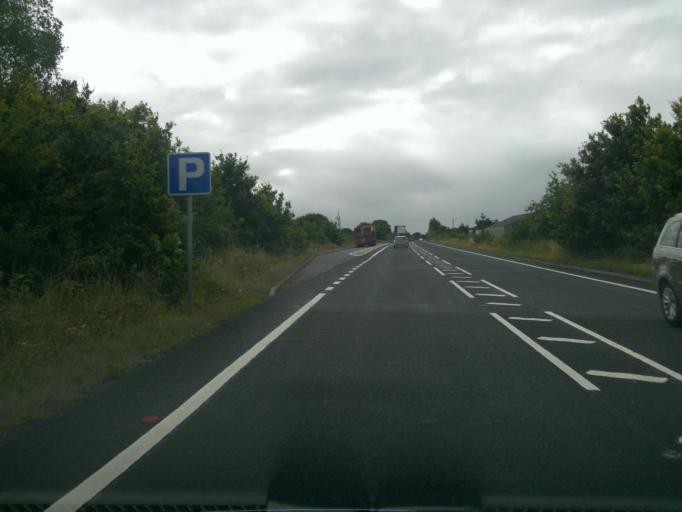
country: GB
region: England
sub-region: Essex
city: Little Clacton
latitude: 51.8361
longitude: 1.1250
